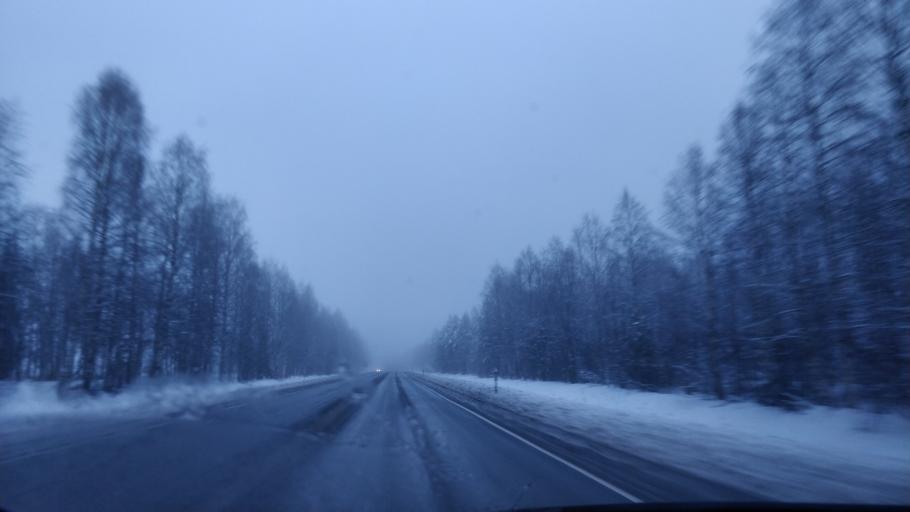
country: FI
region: Lapland
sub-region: Kemi-Tornio
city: Tervola
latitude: 66.1526
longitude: 25.0077
